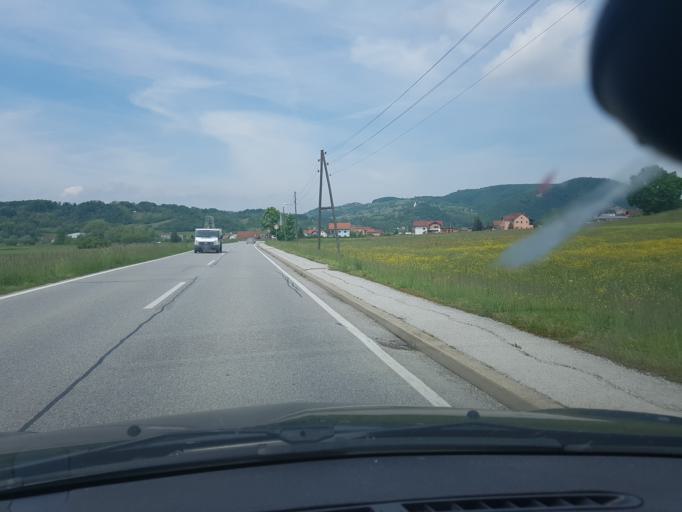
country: HR
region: Krapinsko-Zagorska
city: Pregrada
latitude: 46.1467
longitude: 15.7660
